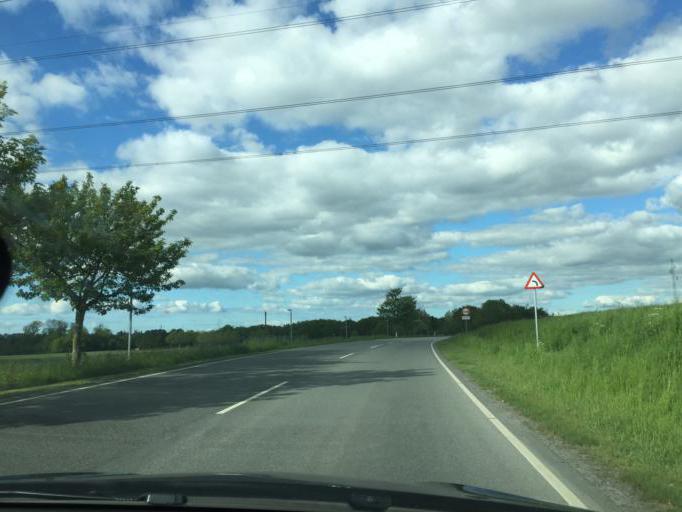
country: DK
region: South Denmark
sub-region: Odense Kommune
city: Bellinge
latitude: 55.3441
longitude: 10.3263
